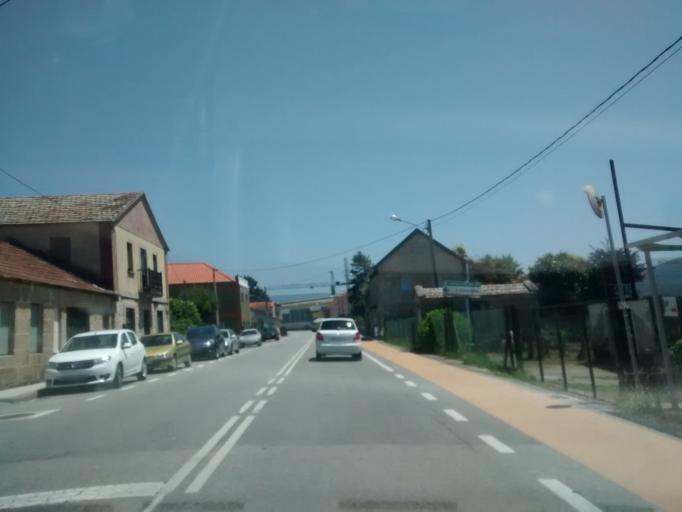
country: ES
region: Galicia
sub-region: Provincia de Pontevedra
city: Nigran
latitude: 42.1149
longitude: -8.8077
